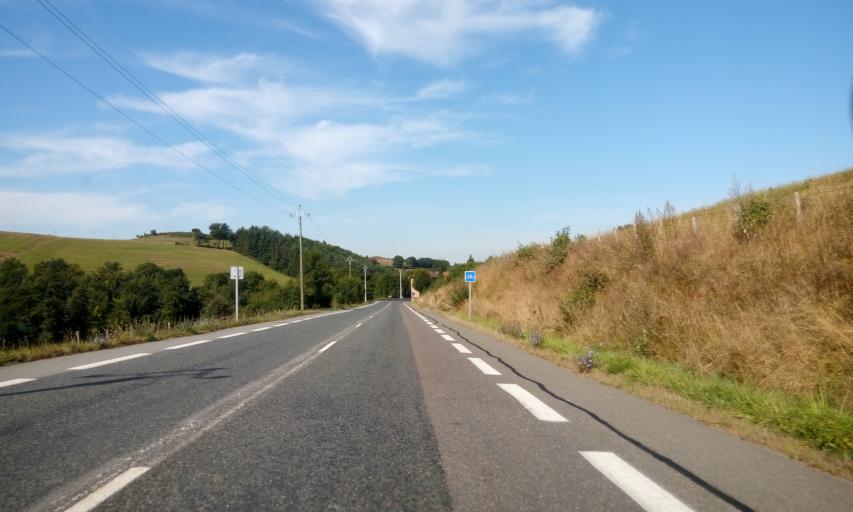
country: FR
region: Rhone-Alpes
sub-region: Departement du Rhone
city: Amplepuis
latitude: 45.9719
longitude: 4.3525
